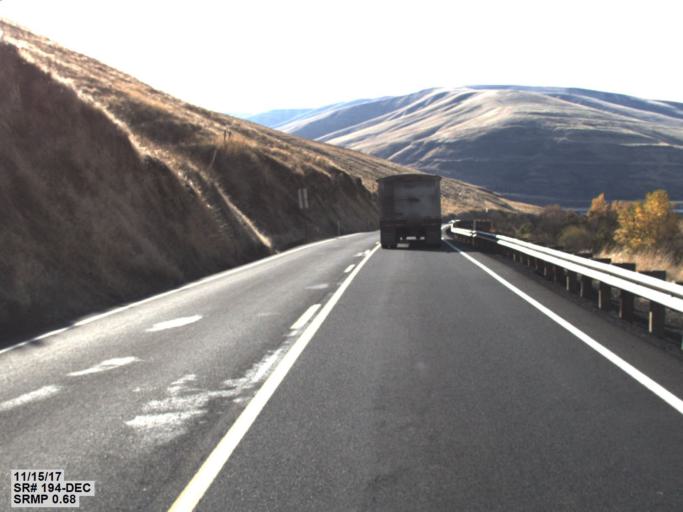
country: US
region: Washington
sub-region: Whitman County
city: Colfax
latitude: 46.7120
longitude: -117.4657
